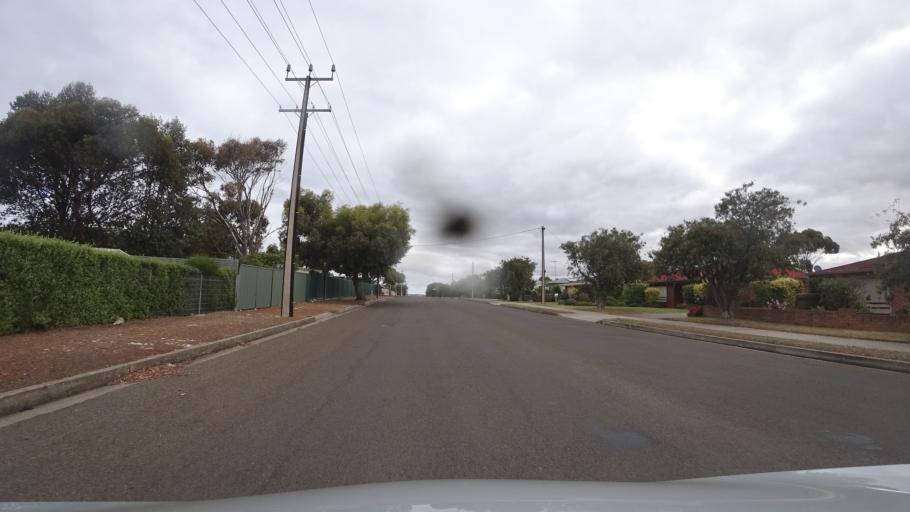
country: AU
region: South Australia
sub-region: Kangaroo Island
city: Kingscote
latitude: -35.6558
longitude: 137.6340
